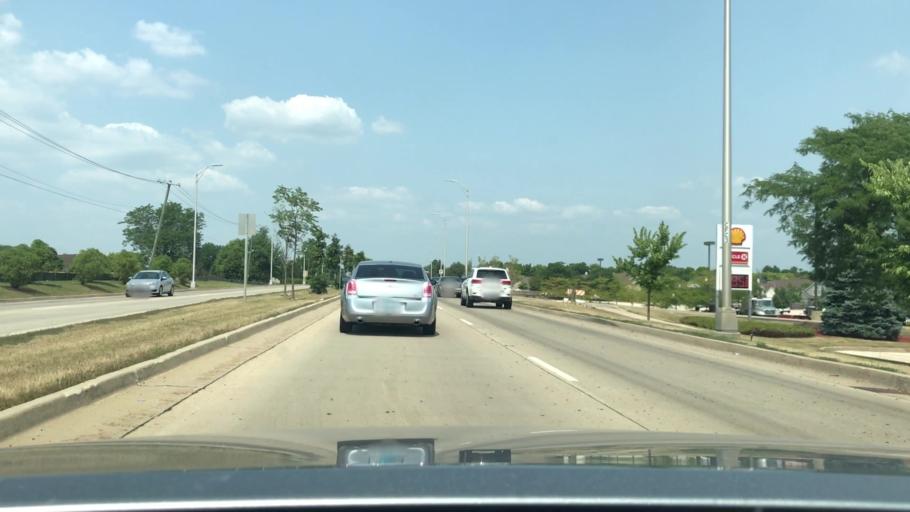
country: US
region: Illinois
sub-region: Will County
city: Crystal Lawns
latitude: 41.5663
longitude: -88.2004
